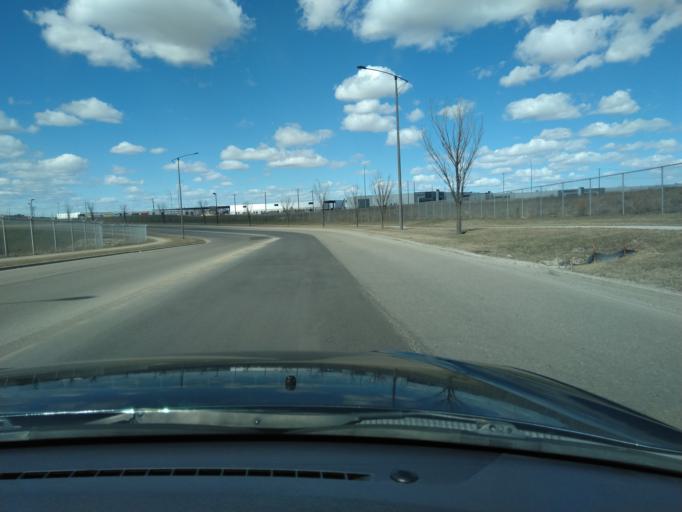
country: CA
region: Alberta
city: Calgary
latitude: 51.1381
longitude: -114.0156
